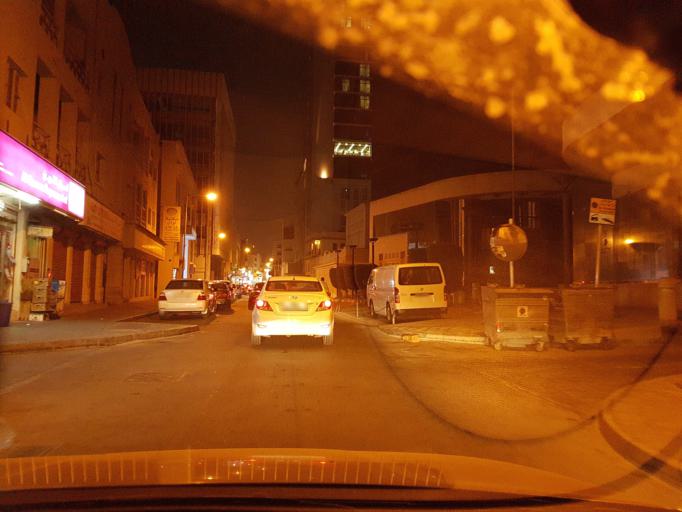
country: BH
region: Manama
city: Manama
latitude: 26.2355
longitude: 50.5783
